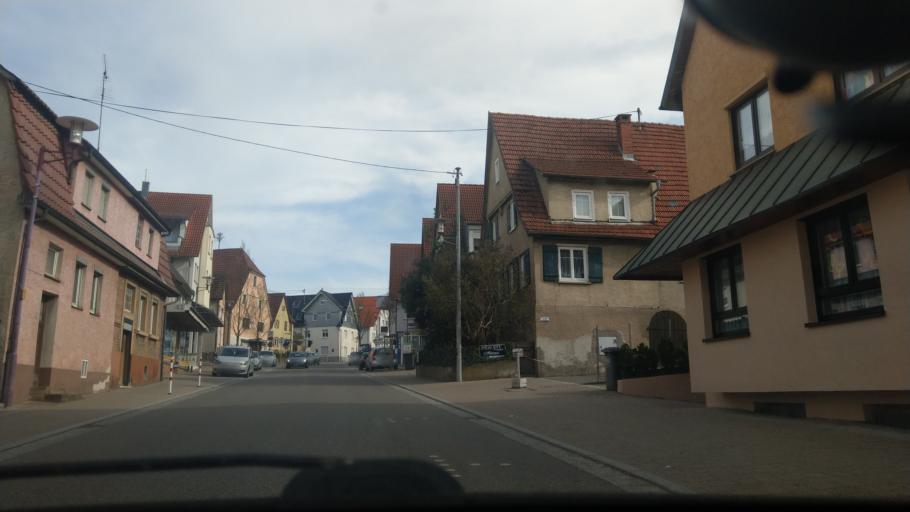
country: DE
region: Baden-Wuerttemberg
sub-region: Regierungsbezirk Stuttgart
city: Filderstadt
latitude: 48.6730
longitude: 9.2392
